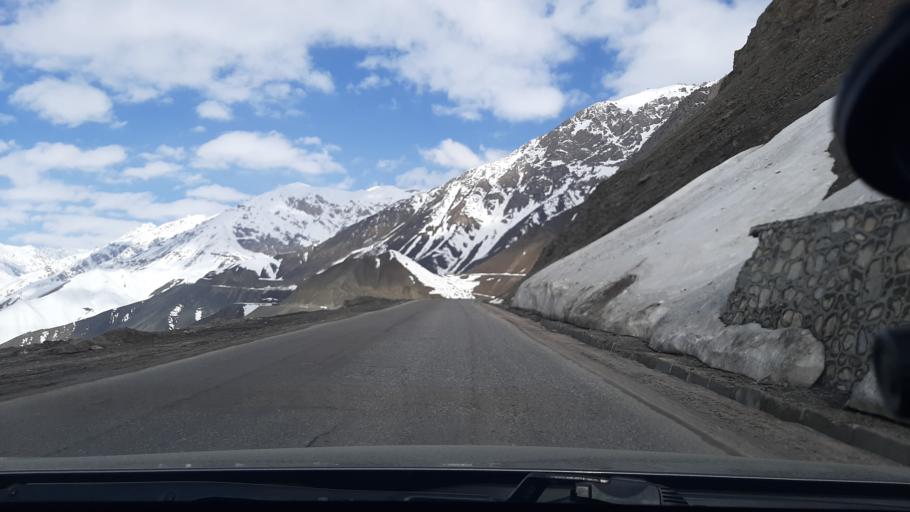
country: TJ
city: Tagob
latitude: 39.0540
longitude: 68.7349
